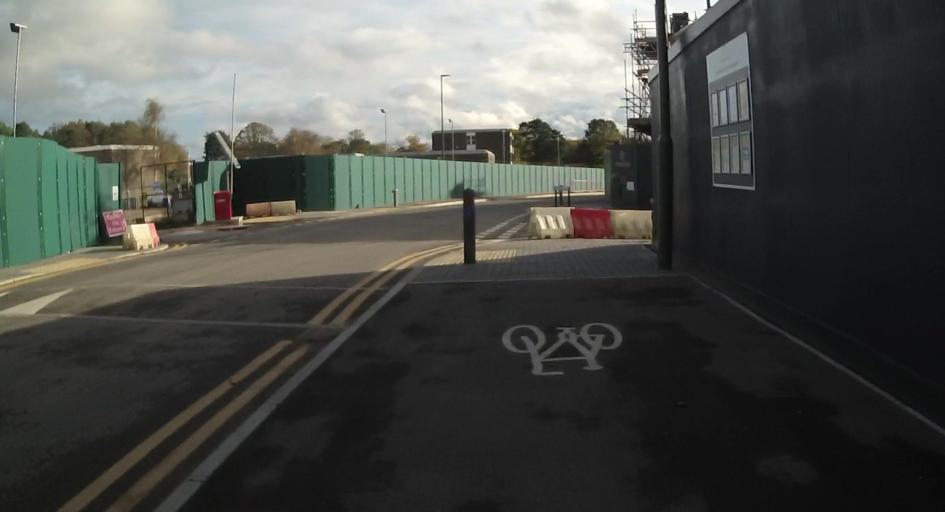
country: GB
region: England
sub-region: Surrey
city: Frimley
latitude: 51.3058
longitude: -0.7038
